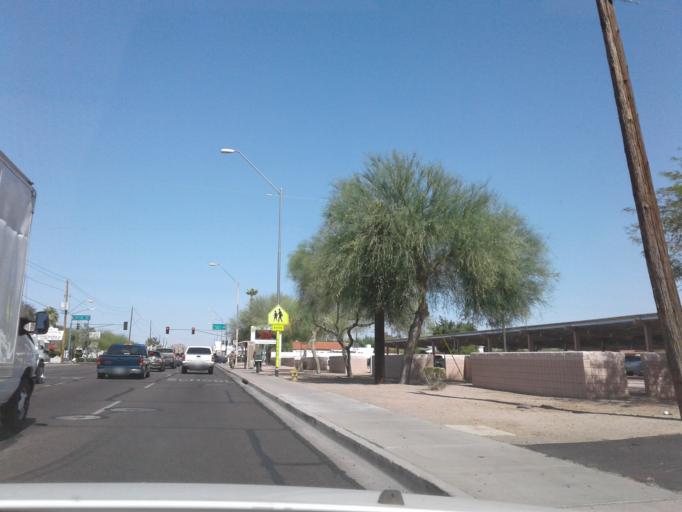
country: US
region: Arizona
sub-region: Maricopa County
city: Phoenix
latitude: 33.4656
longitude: -112.0362
